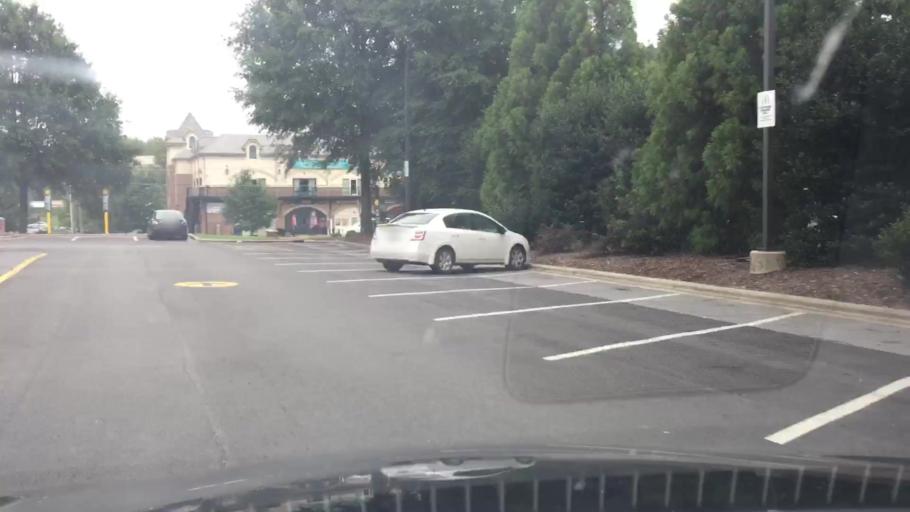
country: US
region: North Carolina
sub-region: Iredell County
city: Mooresville
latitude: 35.5549
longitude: -80.8556
